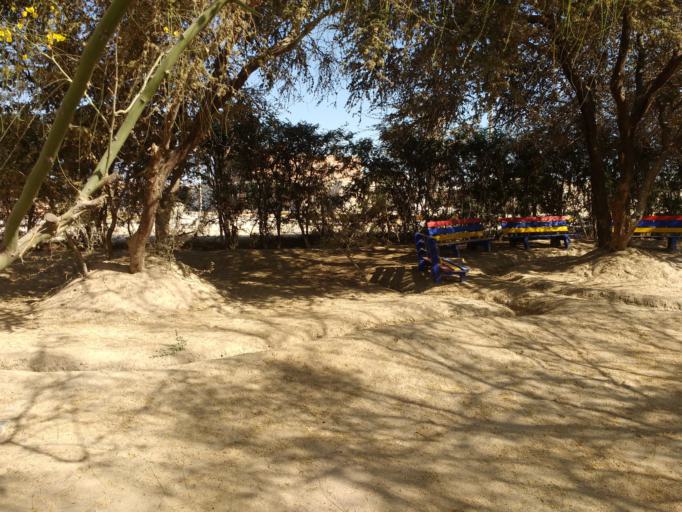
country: PE
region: Ica
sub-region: Provincia de Pisco
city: Villa Tupac Amaru
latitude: -13.8352
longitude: -76.1415
